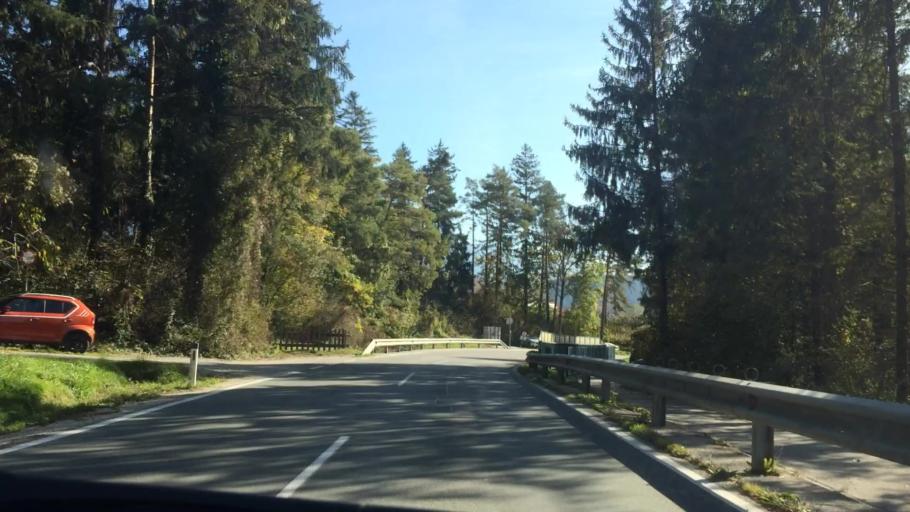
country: AT
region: Tyrol
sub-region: Politischer Bezirk Innsbruck Land
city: Vols
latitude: 47.2657
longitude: 11.3238
